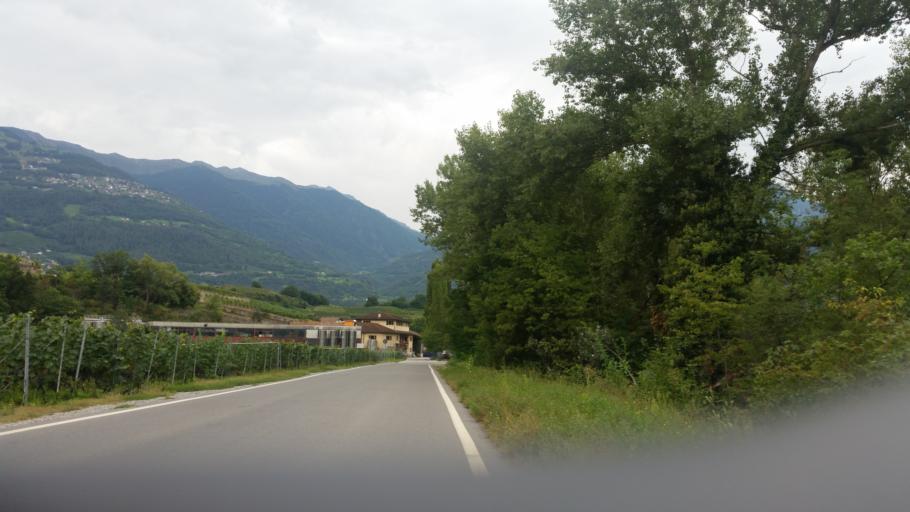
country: CH
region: Valais
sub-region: Conthey District
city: Conthey
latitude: 46.2275
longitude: 7.3133
